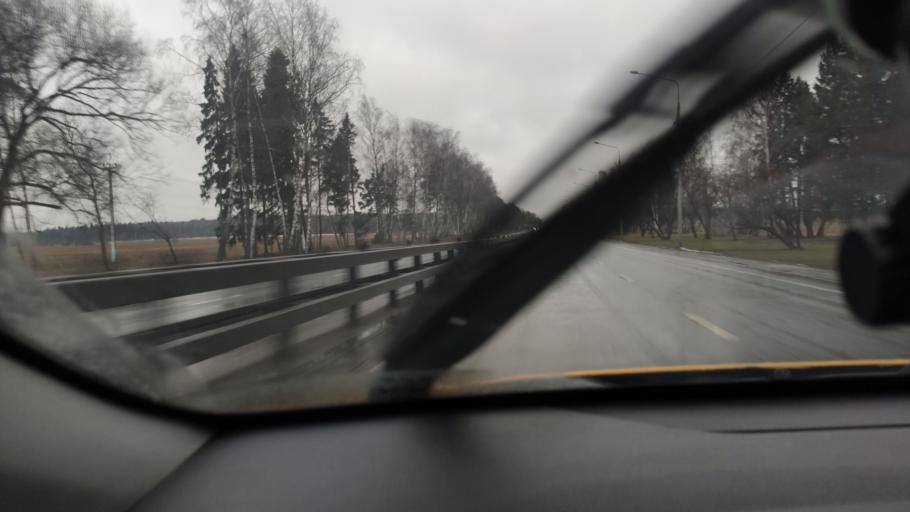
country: RU
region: Moskovskaya
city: Troitsk
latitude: 55.3376
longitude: 37.3011
